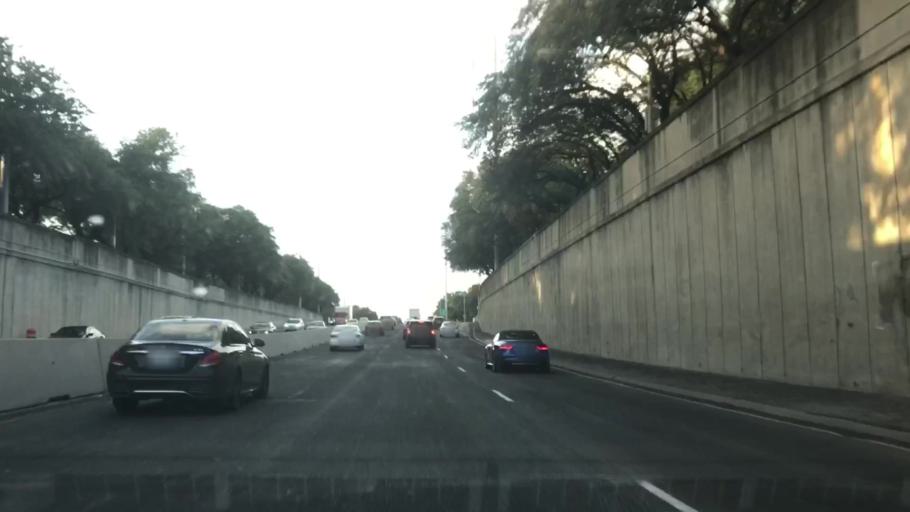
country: US
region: Texas
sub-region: Dallas County
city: University Park
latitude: 32.8324
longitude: -96.8155
